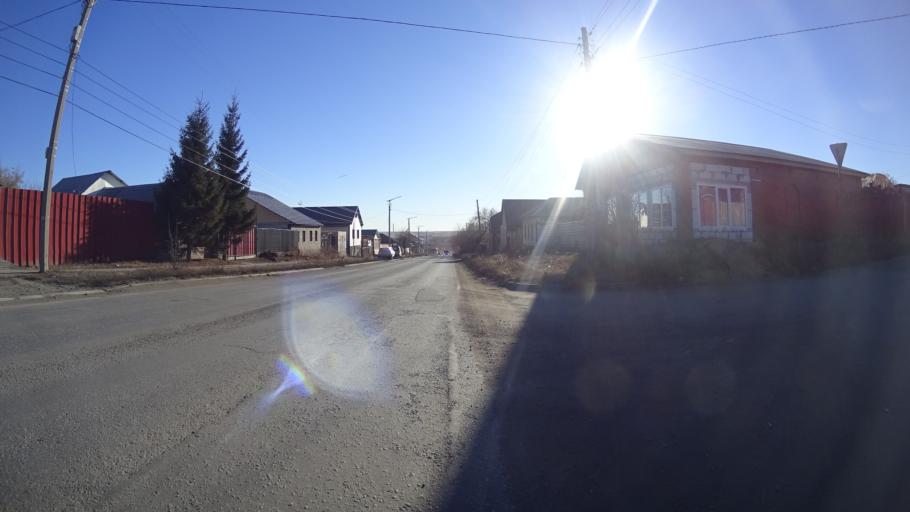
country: RU
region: Chelyabinsk
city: Troitsk
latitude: 54.1023
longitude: 61.5623
